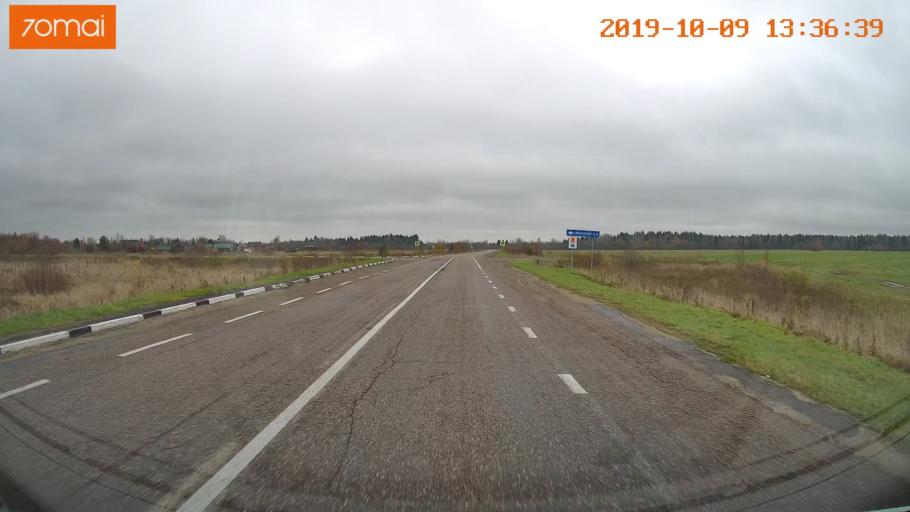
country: RU
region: Jaroslavl
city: Lyubim
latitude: 58.3398
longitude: 41.1017
